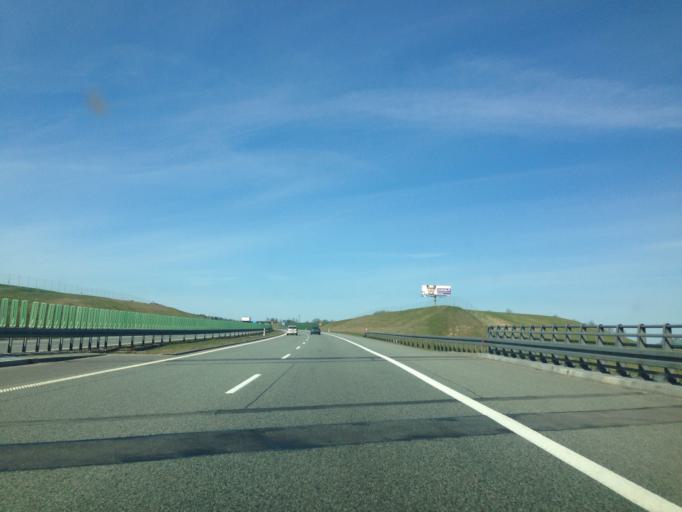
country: PL
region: Pomeranian Voivodeship
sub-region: Powiat starogardzki
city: Bobowo
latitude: 53.8620
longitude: 18.6309
